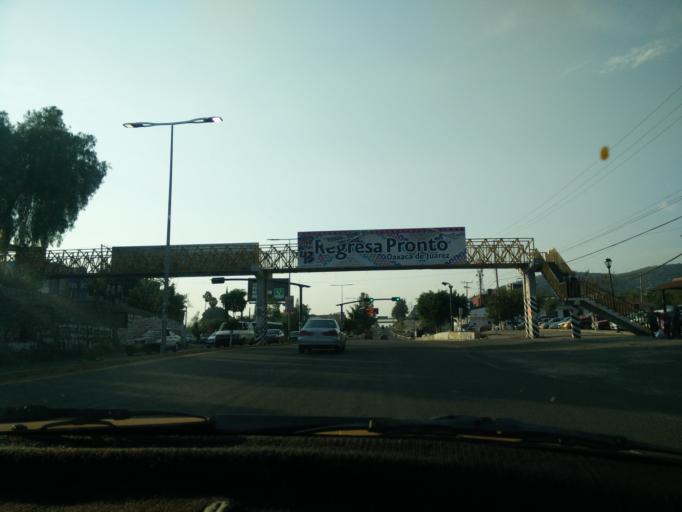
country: MX
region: Oaxaca
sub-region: Santa Maria Atzompa
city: San Jeronimo Yahuiche
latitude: 17.0931
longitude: -96.7480
